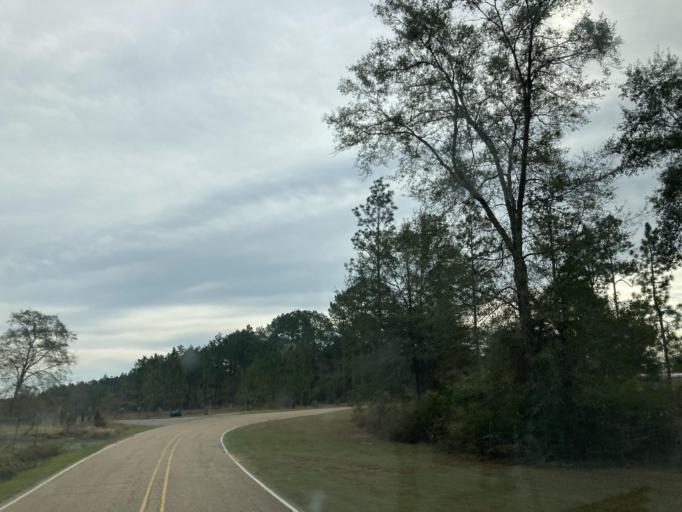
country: US
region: Mississippi
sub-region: Lamar County
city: Purvis
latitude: 31.0985
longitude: -89.4698
